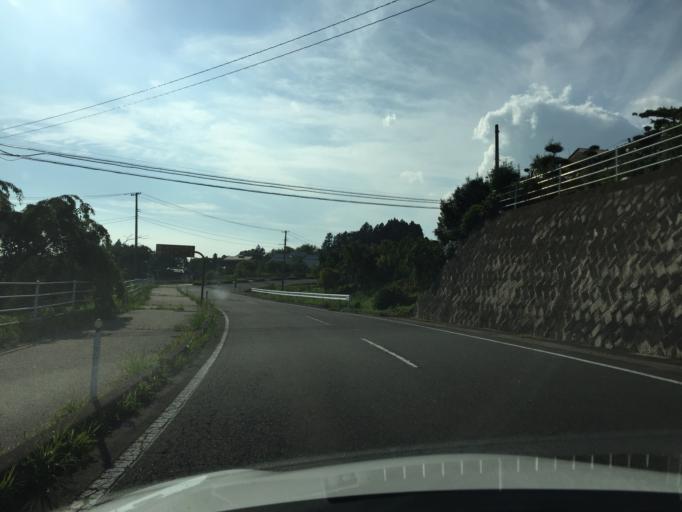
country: JP
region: Fukushima
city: Miharu
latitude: 37.4051
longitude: 140.5026
